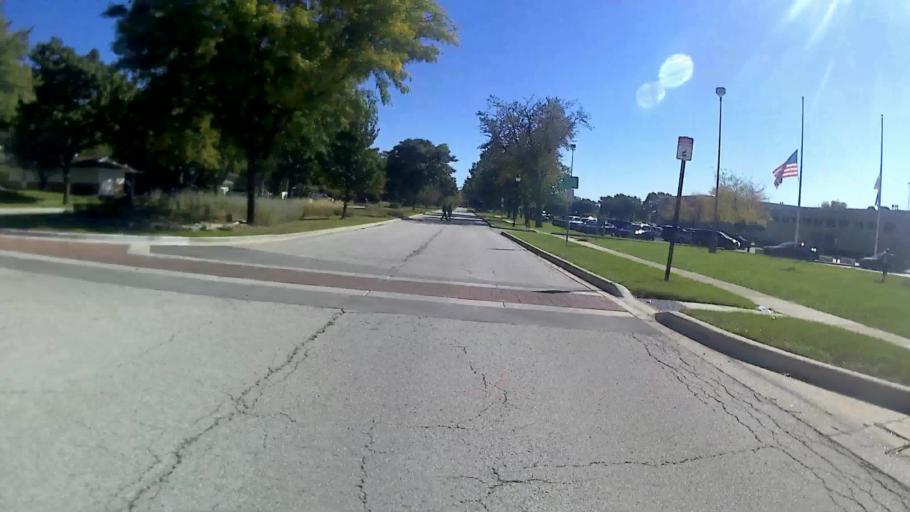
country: US
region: Illinois
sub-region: Cook County
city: Elk Grove Village
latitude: 42.0124
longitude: -87.9969
